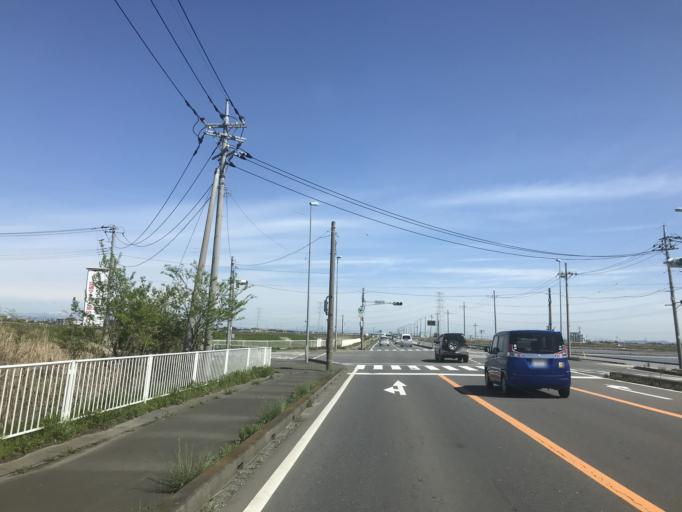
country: JP
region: Ibaraki
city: Ishige
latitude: 36.1141
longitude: 139.9834
